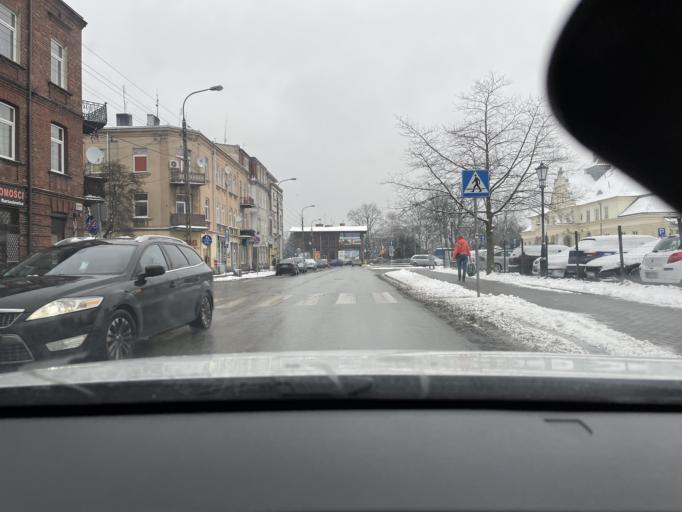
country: PL
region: Masovian Voivodeship
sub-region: Powiat zyrardowski
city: Zyrardow
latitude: 52.0522
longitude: 20.4464
